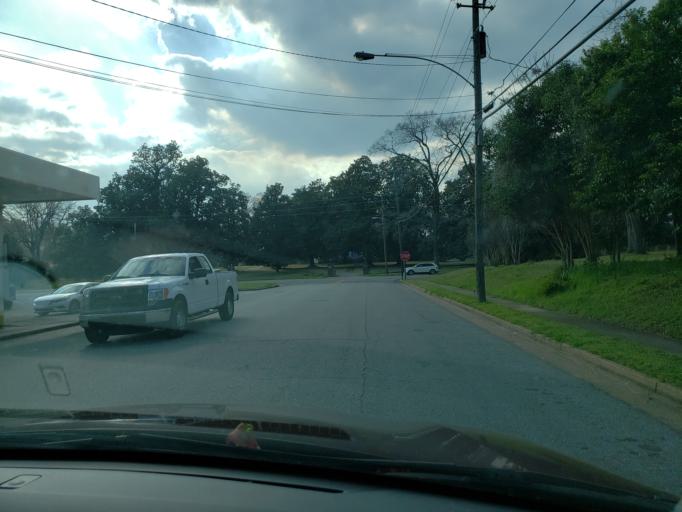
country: US
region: Alabama
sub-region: Hale County
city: Greensboro
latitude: 32.7042
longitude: -87.6062
